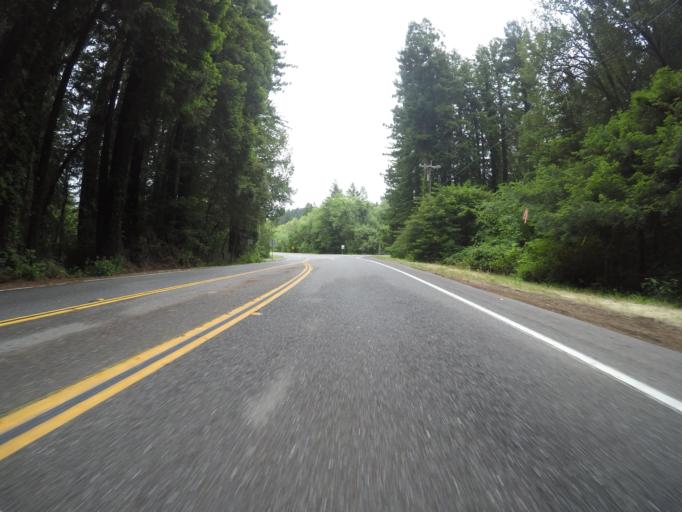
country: US
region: California
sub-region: Humboldt County
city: Rio Dell
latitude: 40.3990
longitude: -123.9478
